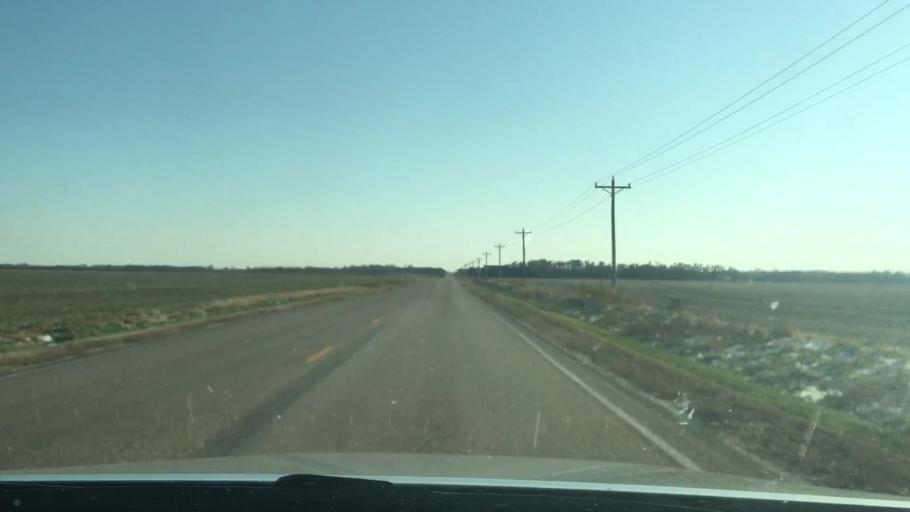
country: US
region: Kansas
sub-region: Reno County
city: Nickerson
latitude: 38.2603
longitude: -98.0877
